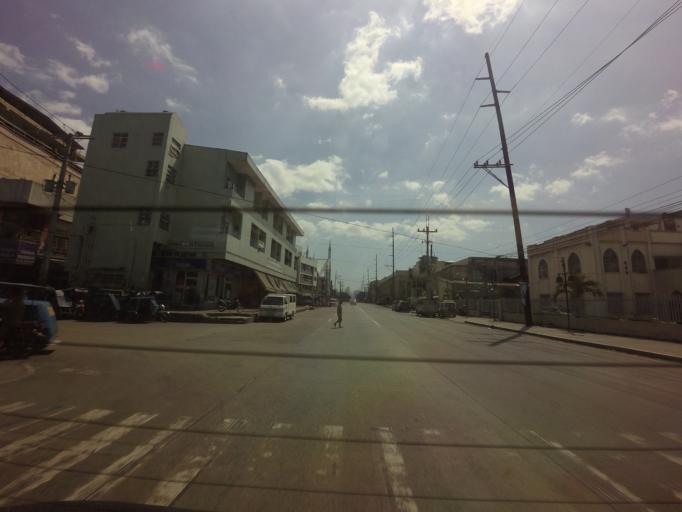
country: PH
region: Metro Manila
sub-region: Caloocan City
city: Niugan
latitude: 14.6342
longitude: 120.9627
